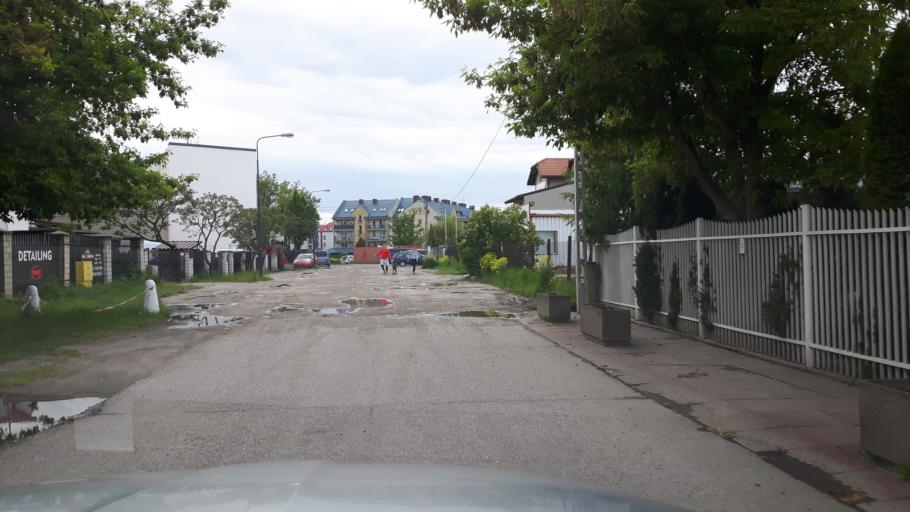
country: PL
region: Masovian Voivodeship
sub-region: Powiat wolominski
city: Zabki
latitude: 52.2888
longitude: 21.0872
